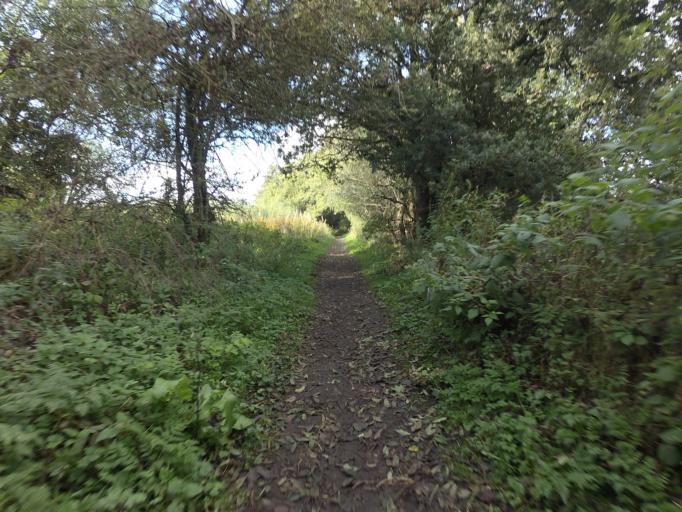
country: GB
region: Scotland
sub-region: West Lothian
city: East Calder
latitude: 55.9058
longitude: -3.4712
